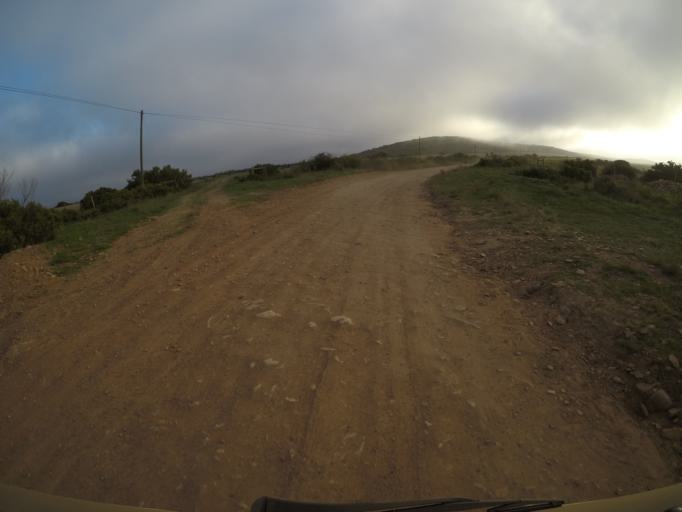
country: ZA
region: Western Cape
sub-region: Eden District Municipality
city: Mossel Bay
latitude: -34.1399
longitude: 22.0401
